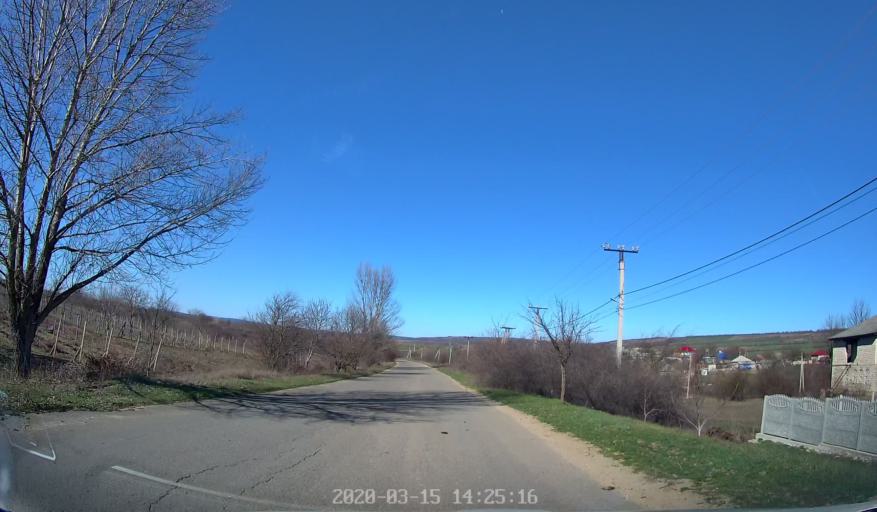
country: MD
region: Orhei
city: Orhei
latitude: 47.3368
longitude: 28.9170
